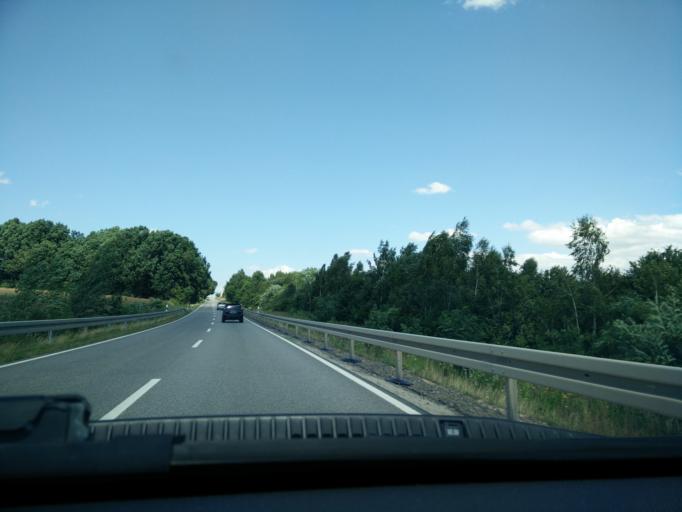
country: DE
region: Saxony
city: Penig
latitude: 50.9593
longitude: 12.6923
